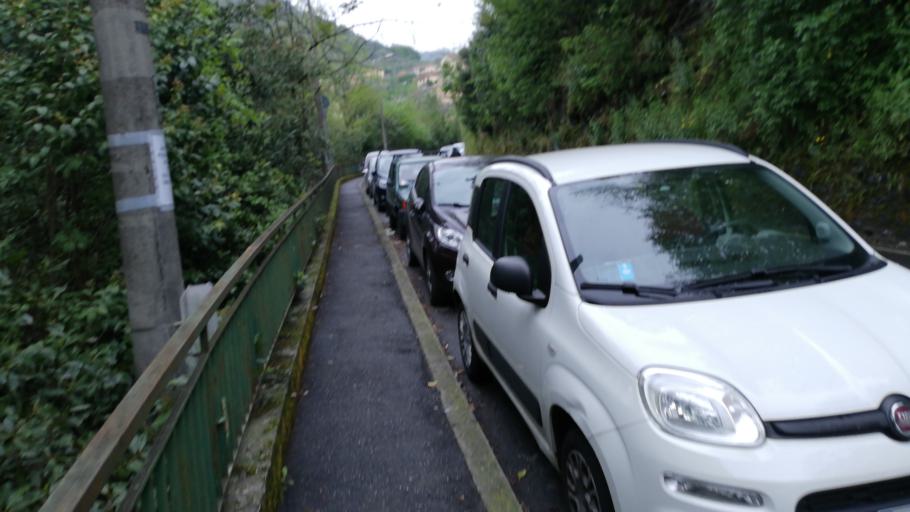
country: IT
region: Liguria
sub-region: Provincia di Genova
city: Piccarello
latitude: 44.4501
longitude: 9.0089
